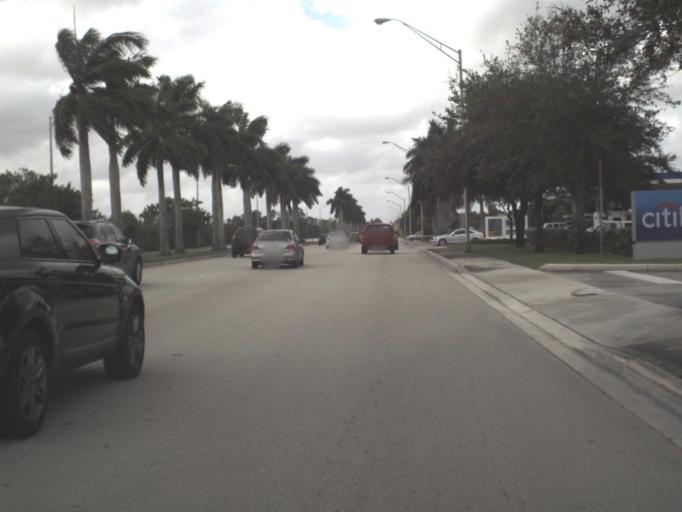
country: US
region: Florida
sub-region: Miami-Dade County
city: Doral
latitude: 25.8118
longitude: -80.3720
